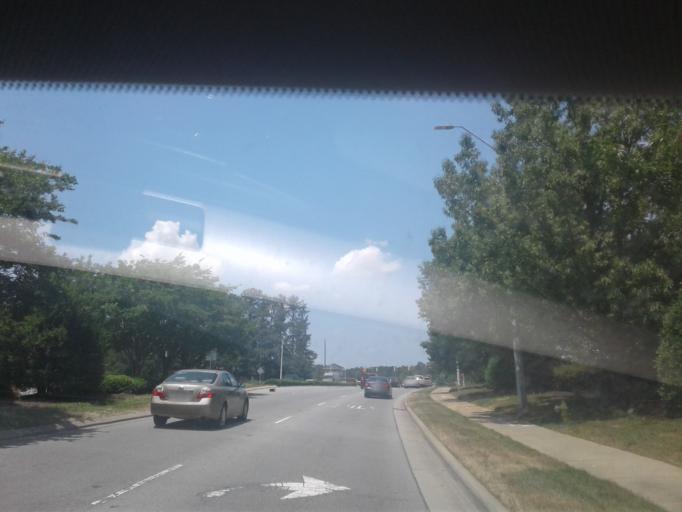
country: US
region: North Carolina
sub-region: Wake County
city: Garner
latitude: 35.6945
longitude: -78.5844
